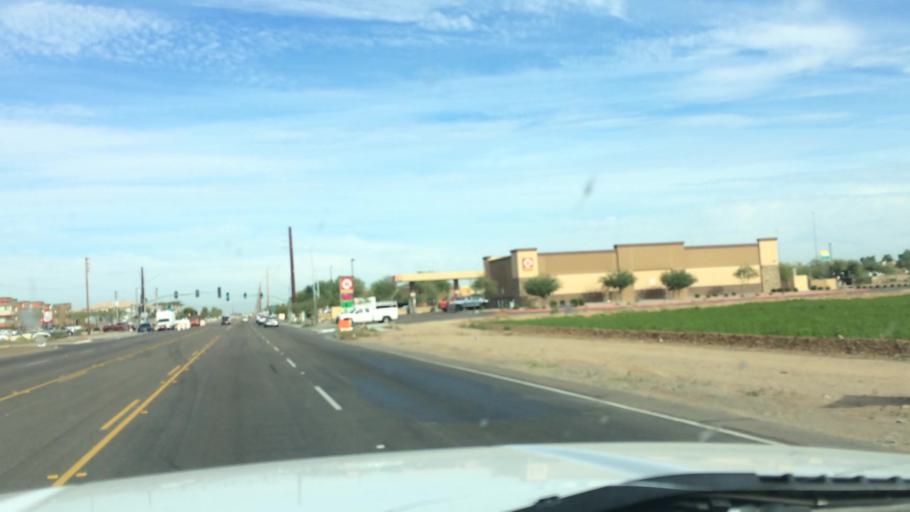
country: US
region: Arizona
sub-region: Maricopa County
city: Tolleson
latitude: 33.5067
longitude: -112.2725
